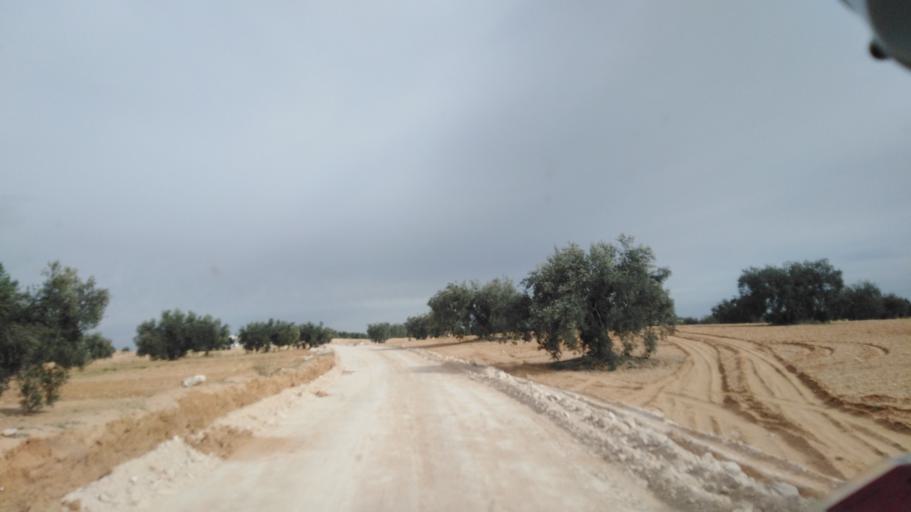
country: TN
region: Safaqis
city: Bi'r `Ali Bin Khalifah
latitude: 34.8121
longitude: 10.3066
